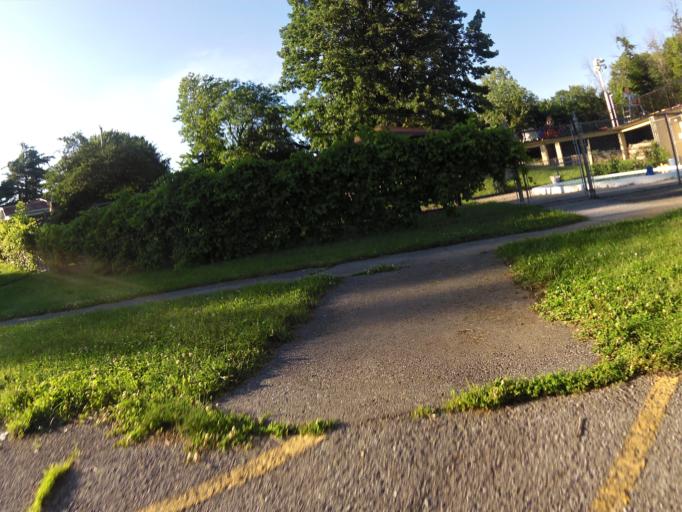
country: CA
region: Ontario
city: Bells Corners
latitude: 45.3459
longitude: -75.8274
